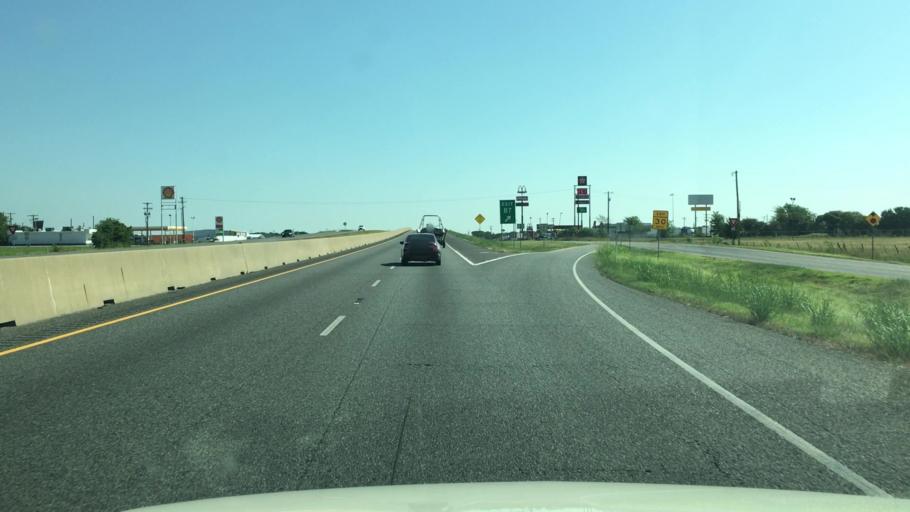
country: US
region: Texas
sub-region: Hunt County
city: Caddo Mills
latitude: 33.0401
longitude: -96.1820
